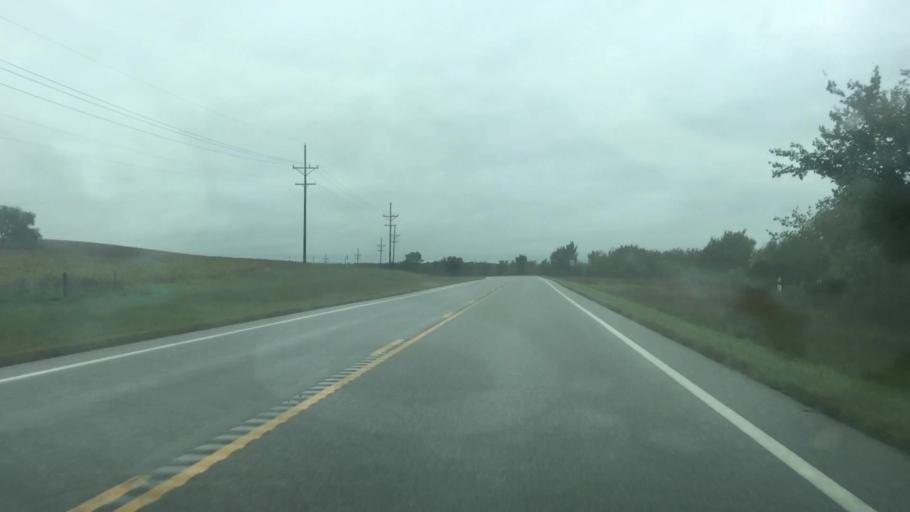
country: US
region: Kansas
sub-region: Anderson County
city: Garnett
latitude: 38.3318
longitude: -95.1773
